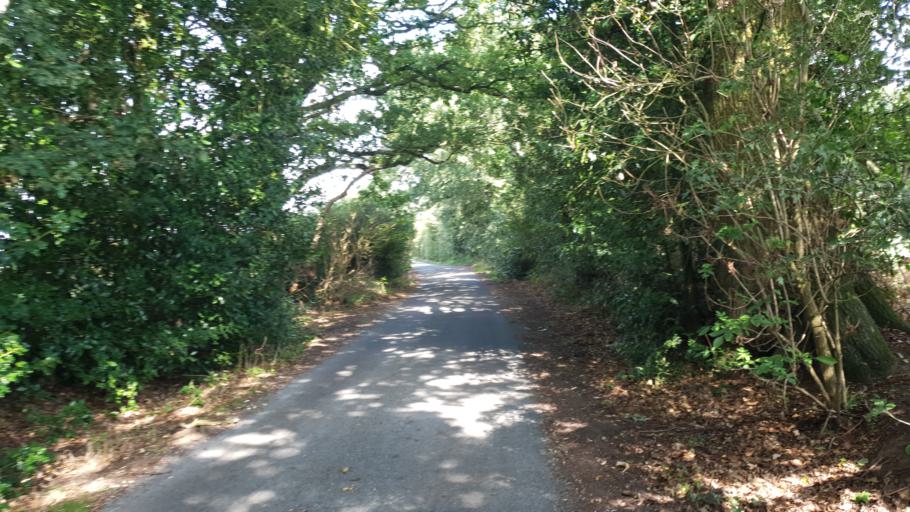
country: GB
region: England
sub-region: Essex
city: Colchester
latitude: 51.9206
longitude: 0.9568
